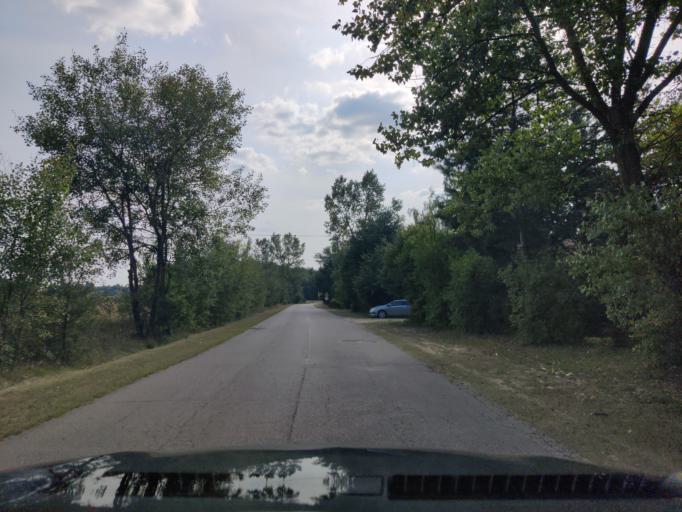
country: PL
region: Masovian Voivodeship
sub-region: Powiat wyszkowski
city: Rzasnik
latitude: 52.7657
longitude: 21.4566
